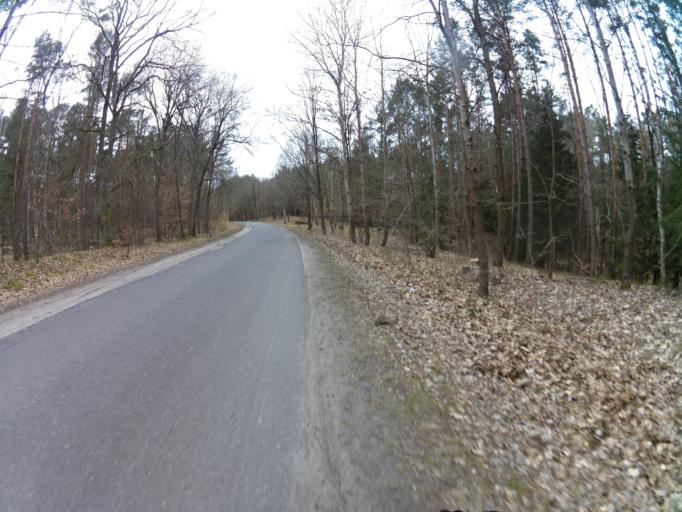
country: PL
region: West Pomeranian Voivodeship
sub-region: Powiat mysliborski
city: Debno
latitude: 52.7438
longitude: 14.7813
